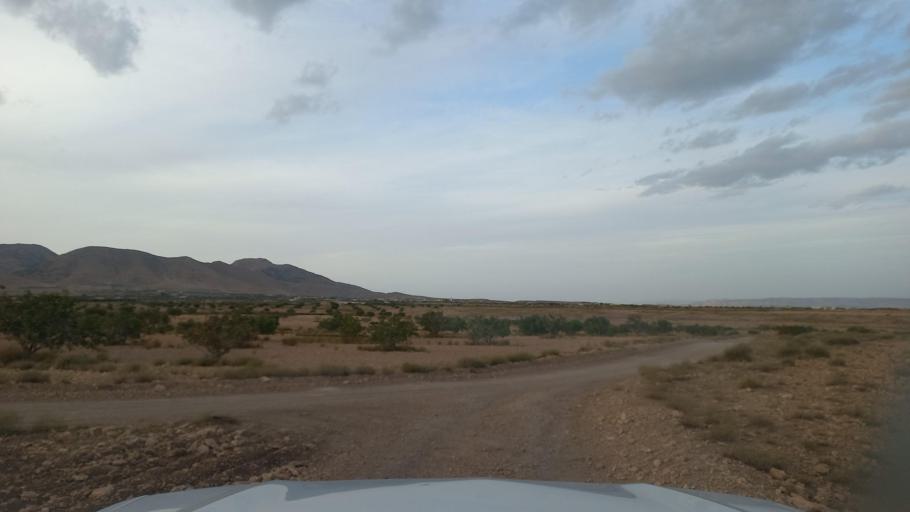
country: TN
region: Al Qasrayn
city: Sbiba
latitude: 35.4253
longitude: 9.0778
